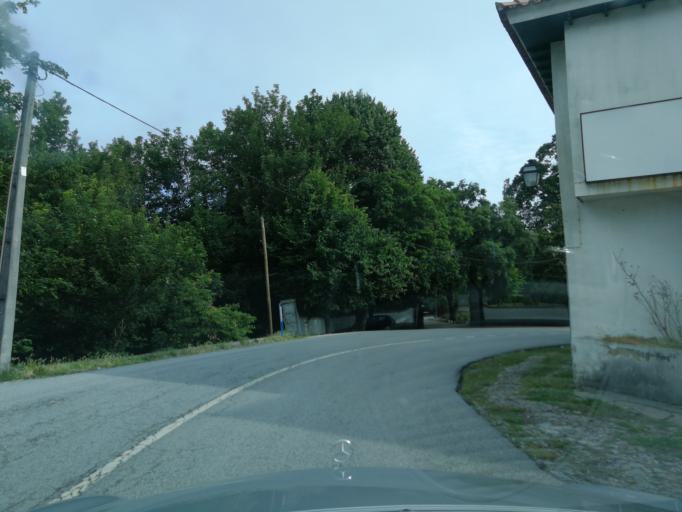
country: PT
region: Braga
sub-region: Braga
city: Adaufe
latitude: 41.5518
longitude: -8.3756
